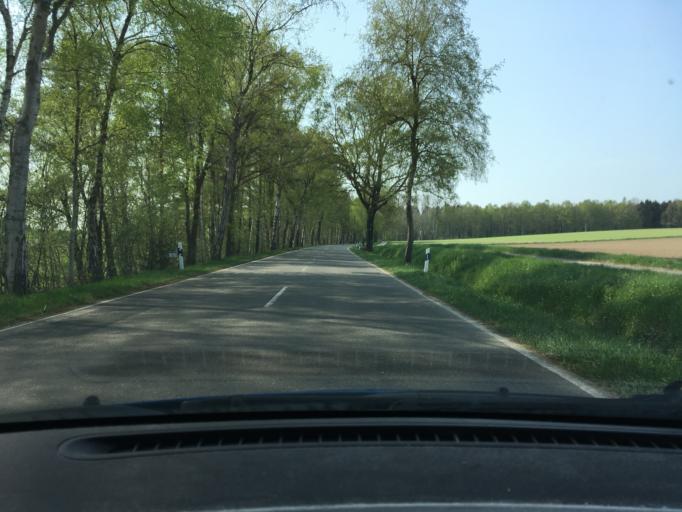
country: DE
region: Lower Saxony
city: Hermannsburg
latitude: 52.8206
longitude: 10.0401
